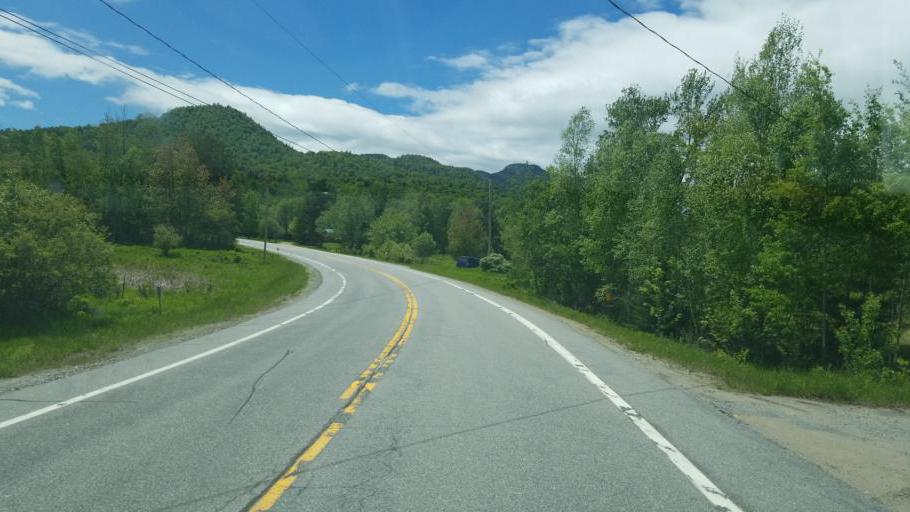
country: US
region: New York
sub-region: Hamilton County
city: Lake Pleasant
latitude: 43.7105
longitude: -74.3293
